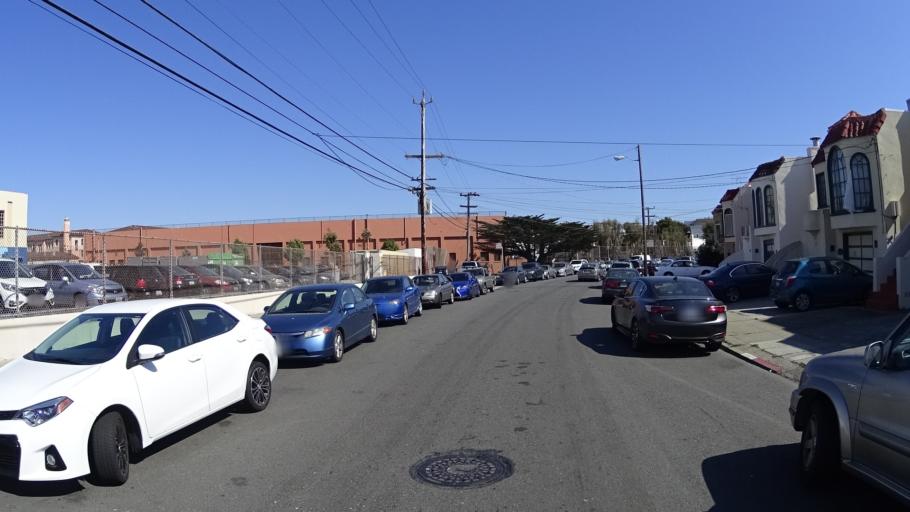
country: US
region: California
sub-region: San Mateo County
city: Daly City
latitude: 37.7207
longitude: -122.4435
